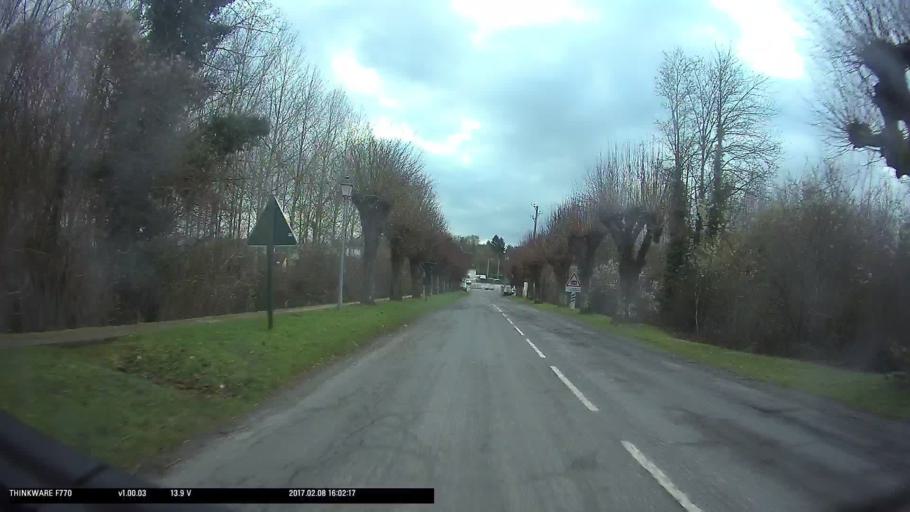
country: FR
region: Ile-de-France
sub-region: Departement du Val-d'Oise
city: Us
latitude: 49.1022
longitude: 1.9714
